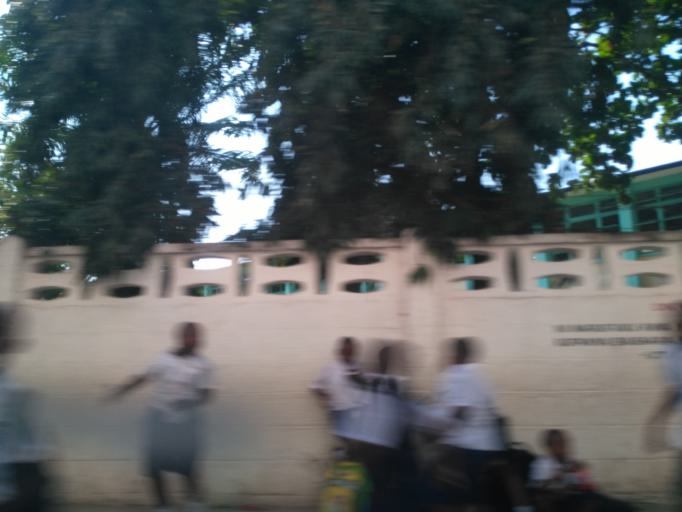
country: TZ
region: Dar es Salaam
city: Dar es Salaam
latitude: -6.8079
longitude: 39.2818
